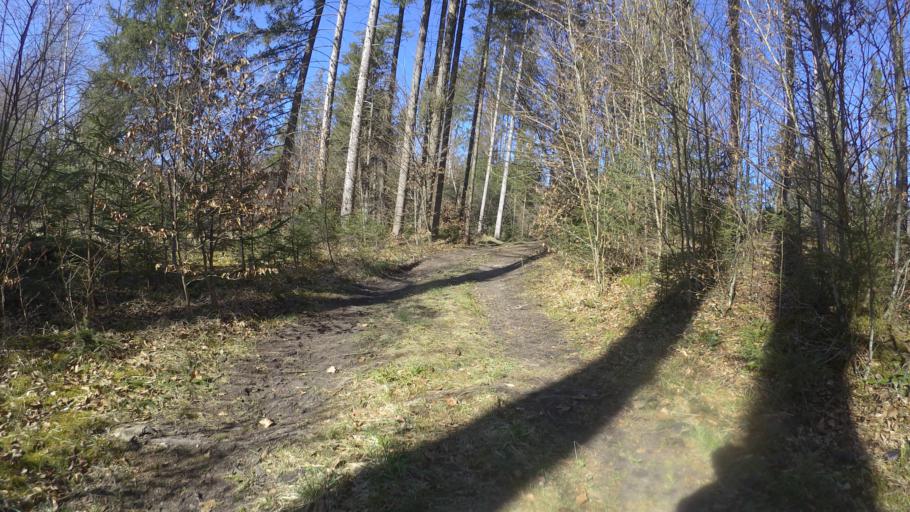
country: DE
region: Bavaria
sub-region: Upper Bavaria
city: Seeon-Seebruck
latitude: 47.9657
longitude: 12.4870
